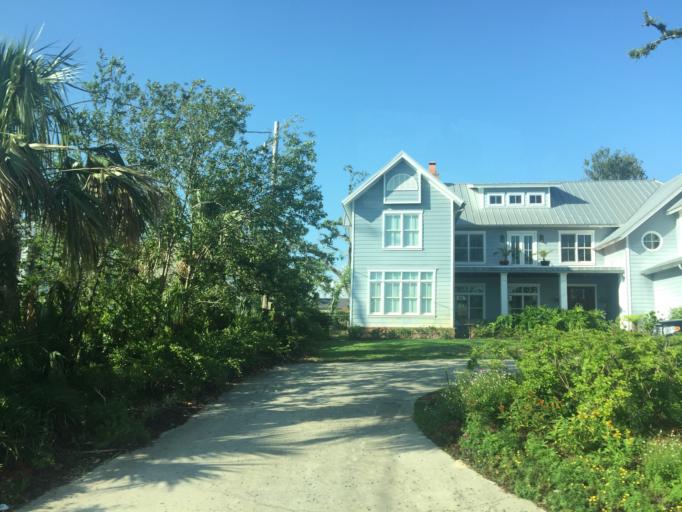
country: US
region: Florida
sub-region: Bay County
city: Panama City
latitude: 30.1435
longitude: -85.6495
